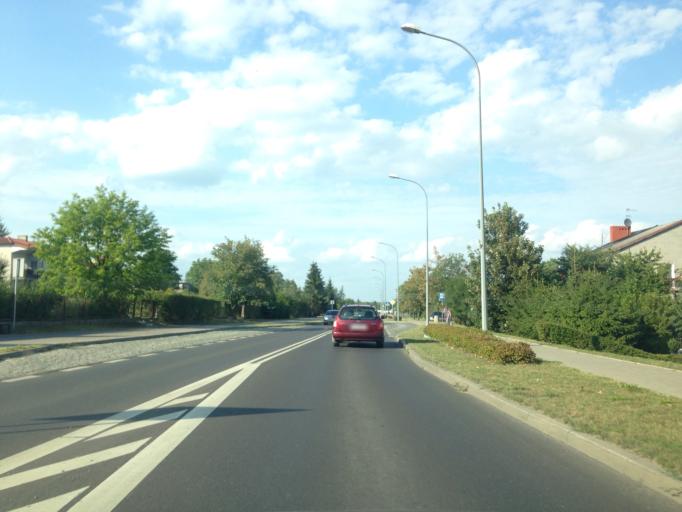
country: PL
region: Warmian-Masurian Voivodeship
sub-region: Powiat ilawski
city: Ilawa
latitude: 53.6079
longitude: 19.5691
